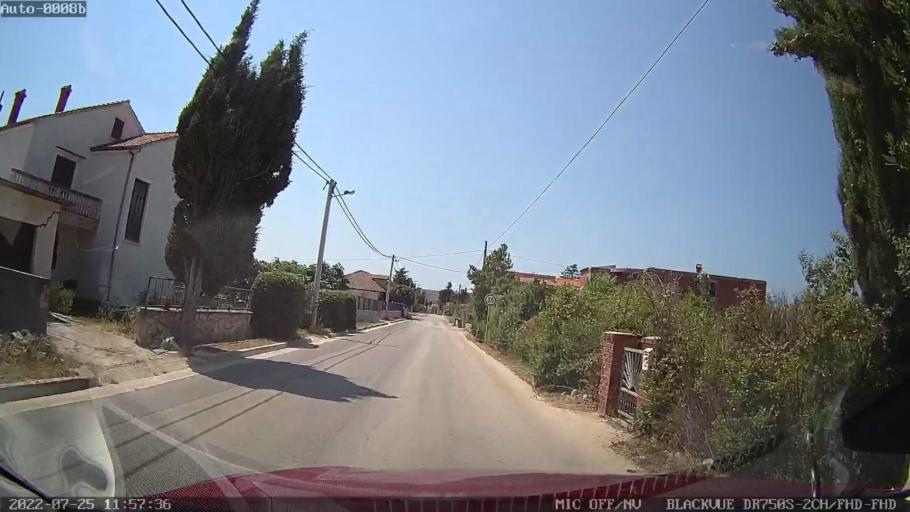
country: HR
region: Zadarska
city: Vrsi
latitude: 44.2420
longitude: 15.2136
